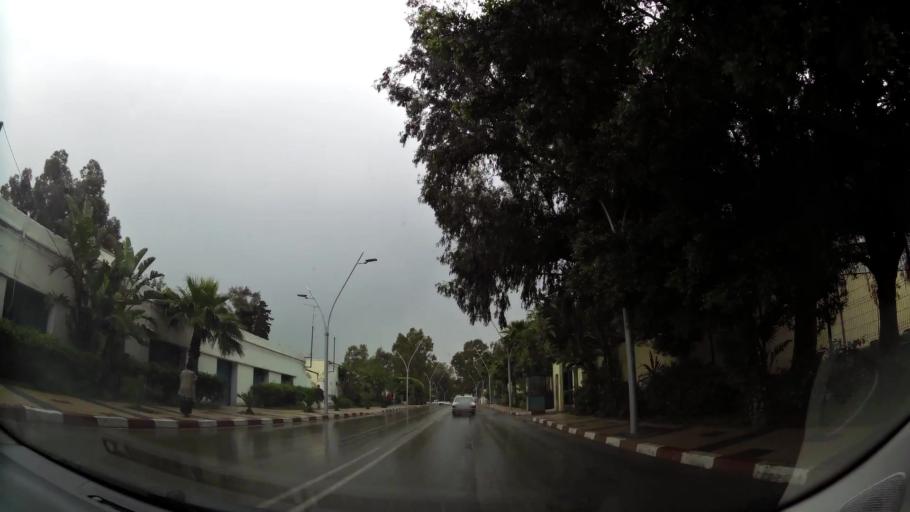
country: MA
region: Oriental
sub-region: Nador
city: Nador
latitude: 35.1550
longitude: -3.0003
